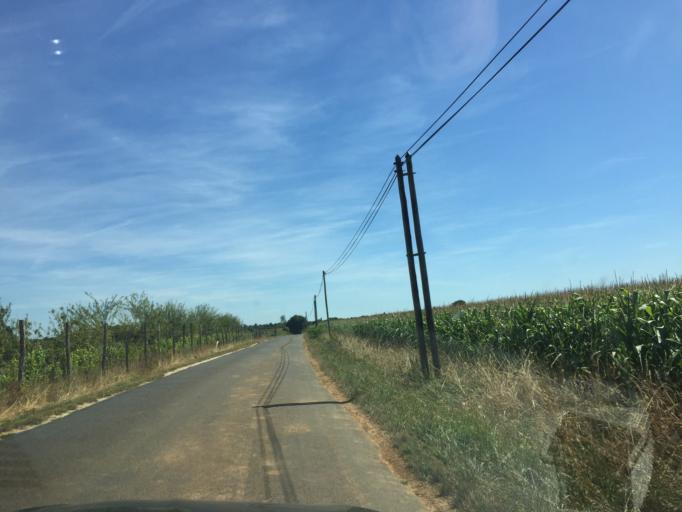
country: FR
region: Poitou-Charentes
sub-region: Departement de la Vienne
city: Iteuil
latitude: 46.4391
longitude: 0.3190
